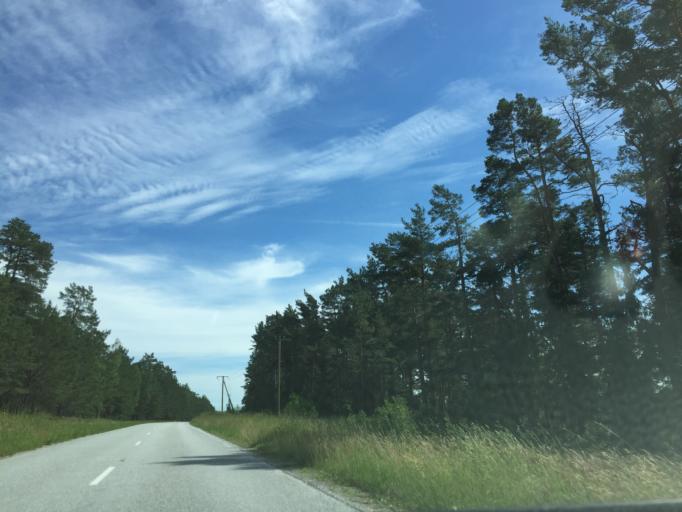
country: LV
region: Talsu Rajons
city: Valdemarpils
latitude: 57.5872
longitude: 22.6144
